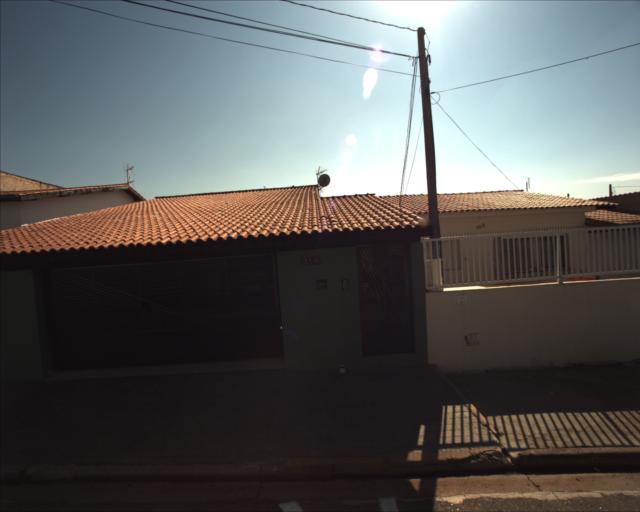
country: BR
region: Sao Paulo
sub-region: Sorocaba
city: Sorocaba
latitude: -23.4803
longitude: -47.4850
